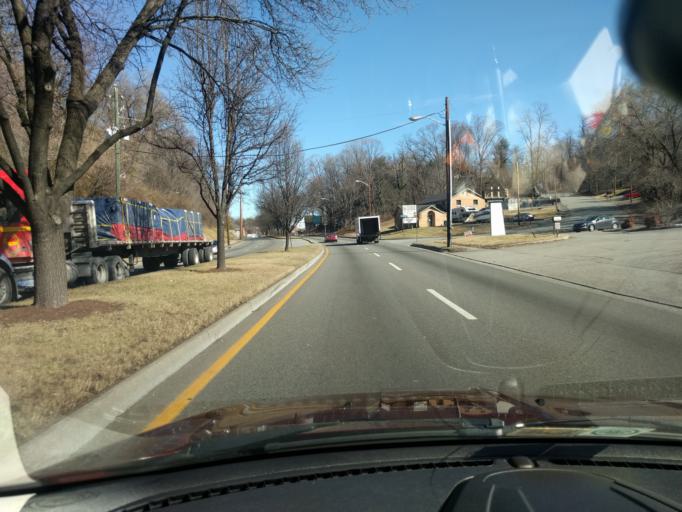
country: US
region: Virginia
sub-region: Roanoke County
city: Vinton
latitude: 37.2867
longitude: -79.9146
